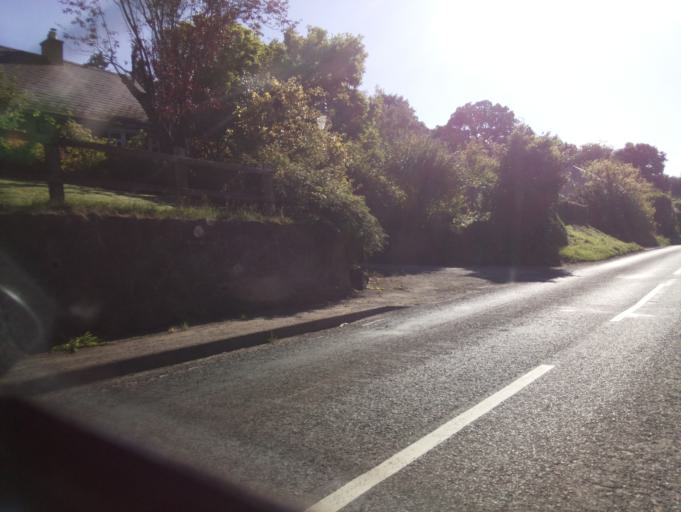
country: GB
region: England
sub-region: Herefordshire
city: Walford
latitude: 51.8661
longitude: -2.6075
